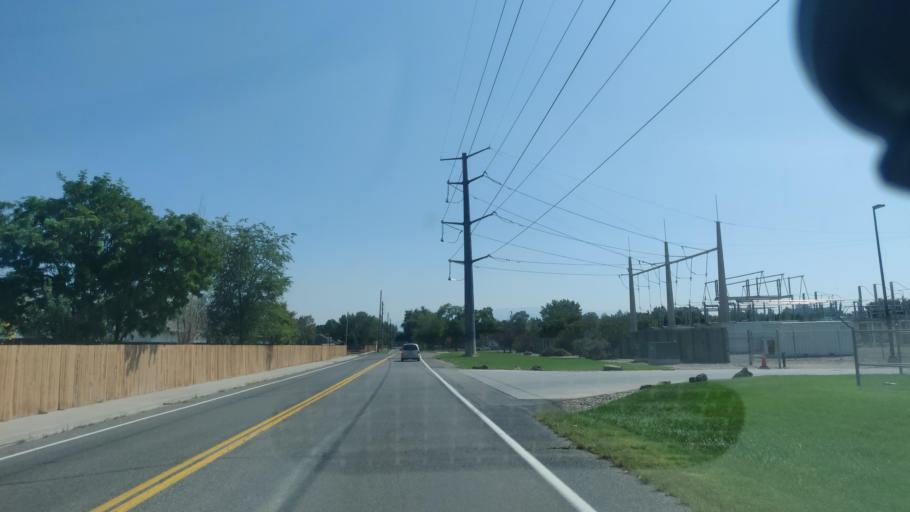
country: US
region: Colorado
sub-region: Mesa County
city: Grand Junction
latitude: 39.0991
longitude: -108.5820
